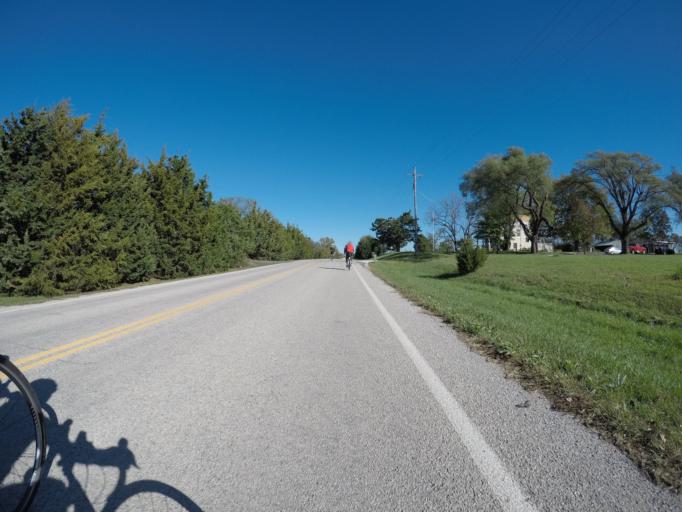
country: US
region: Kansas
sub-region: Johnson County
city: De Soto
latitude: 39.0148
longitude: -94.9739
